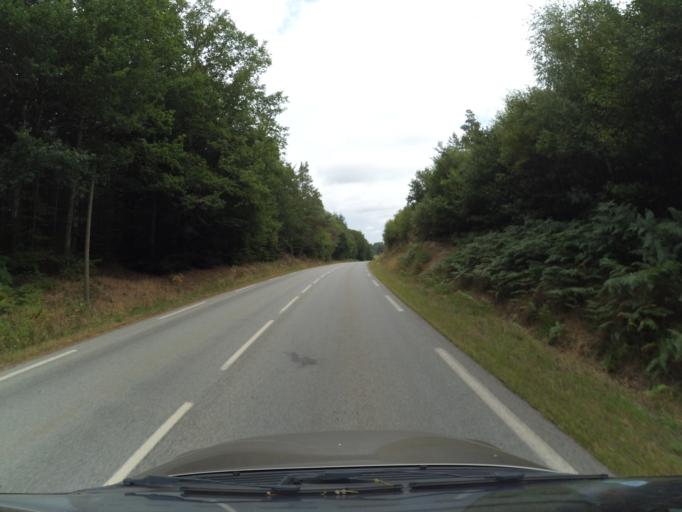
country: FR
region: Limousin
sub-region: Departement de la Correze
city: Ussel
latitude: 45.5936
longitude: 2.2903
